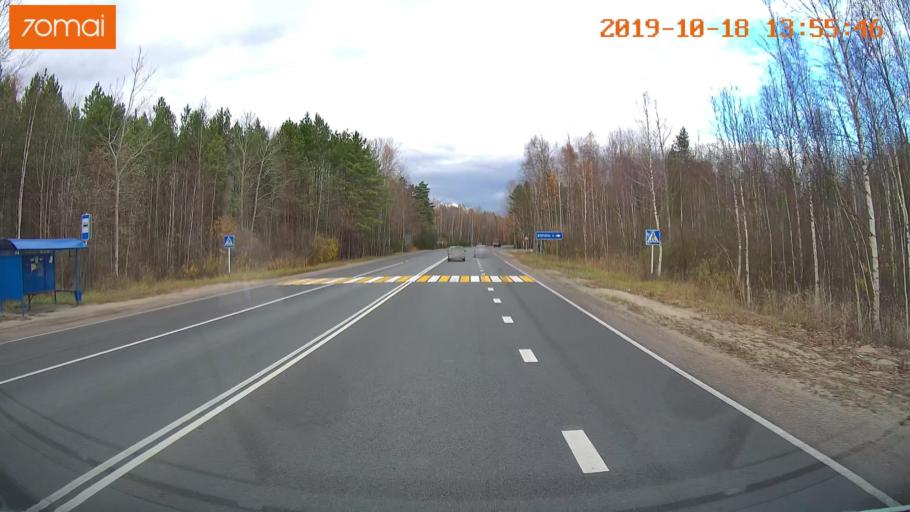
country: RU
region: Rjazan
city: Spas-Klepiki
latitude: 55.0559
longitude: 40.0248
